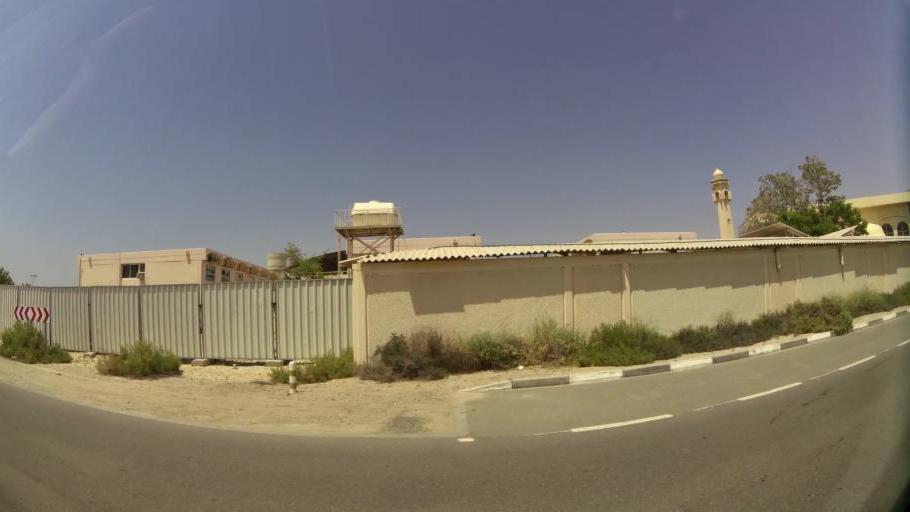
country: AE
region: Ash Shariqah
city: Sharjah
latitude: 25.2946
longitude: 55.3442
